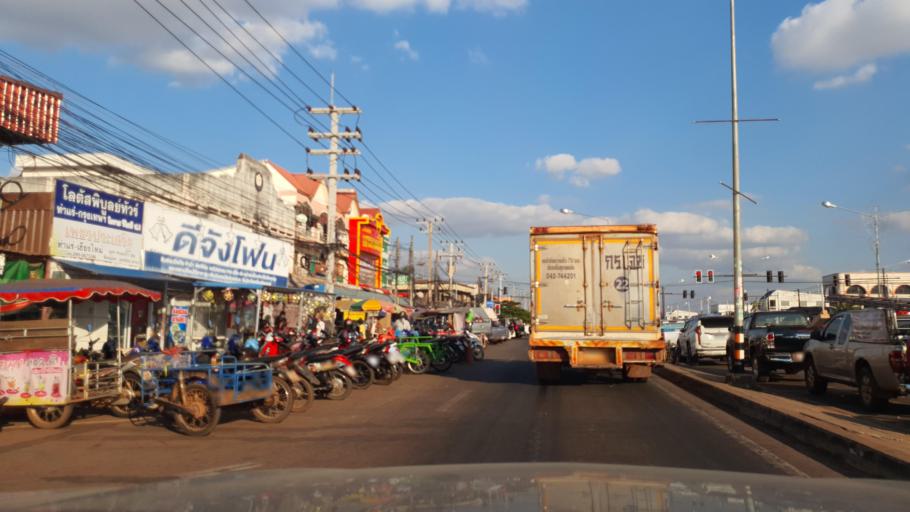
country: TH
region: Sakon Nakhon
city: Sakon Nakhon
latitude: 17.2561
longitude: 104.1871
